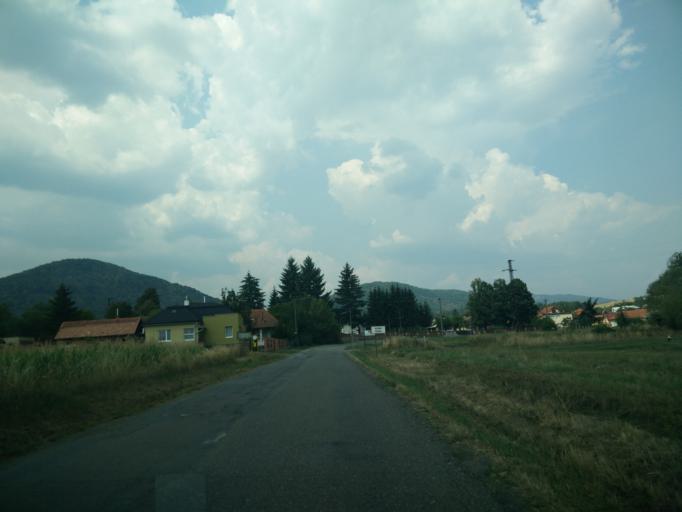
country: SK
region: Banskobystricky
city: Zarnovica
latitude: 48.5636
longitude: 18.7521
